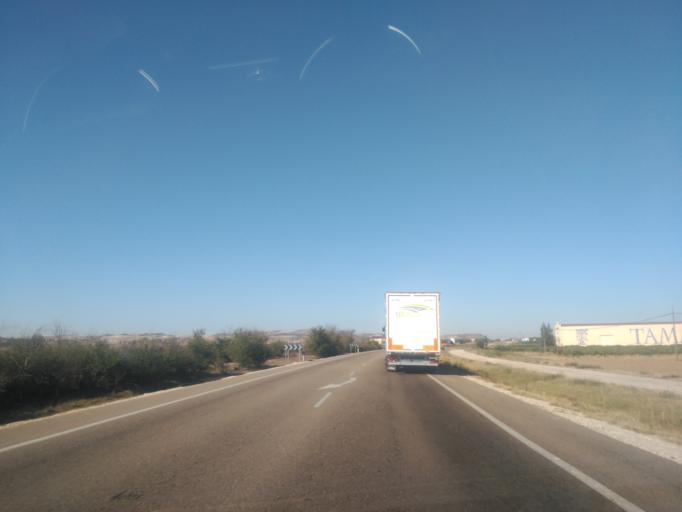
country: ES
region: Castille and Leon
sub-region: Provincia de Valladolid
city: Penafiel
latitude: 41.6080
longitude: -4.1481
